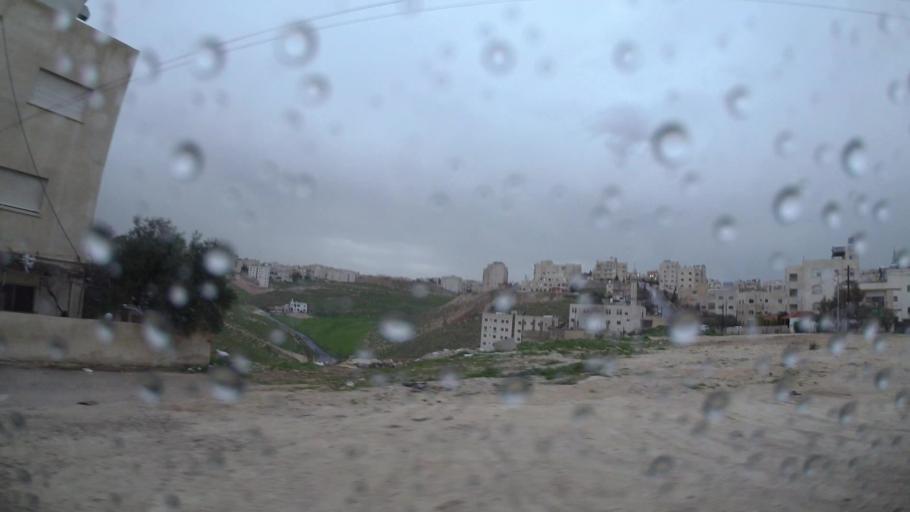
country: JO
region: Amman
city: Amman
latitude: 31.9975
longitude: 35.9678
